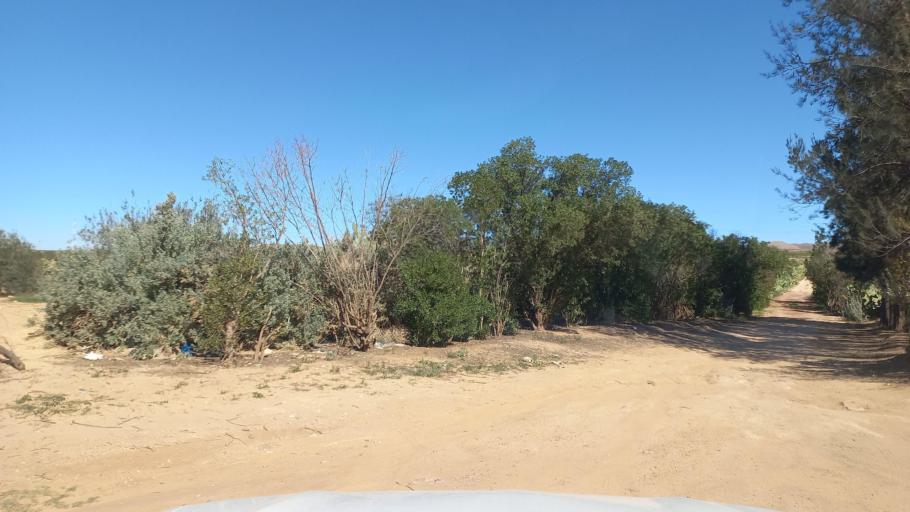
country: TN
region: Al Qasrayn
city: Sbiba
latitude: 35.3629
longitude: 9.0928
